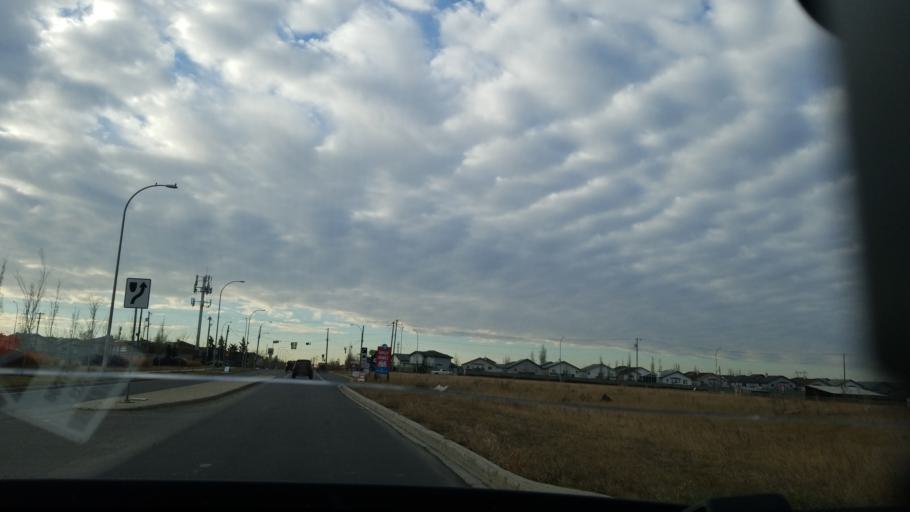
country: CA
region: Alberta
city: Edmonton
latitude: 53.6303
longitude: -113.4429
